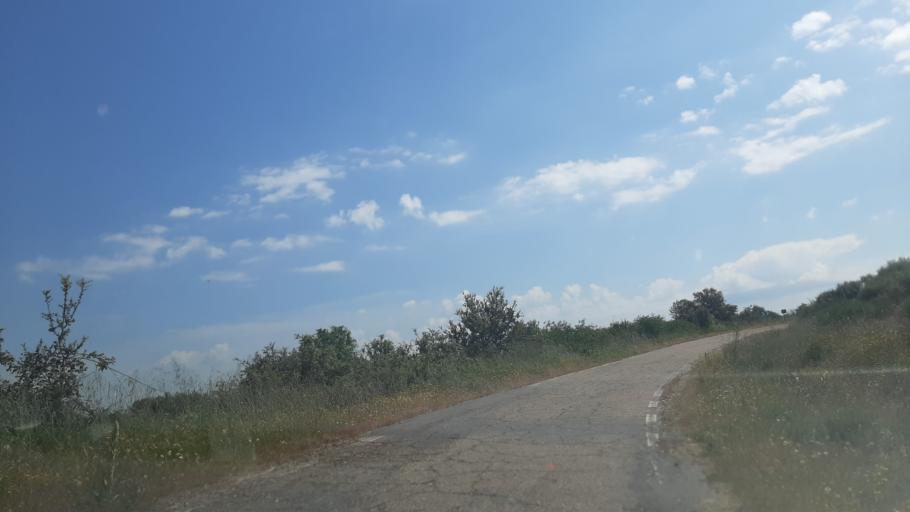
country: ES
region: Castille and Leon
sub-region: Provincia de Salamanca
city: Aldea del Obispo
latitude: 40.6549
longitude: -6.7770
